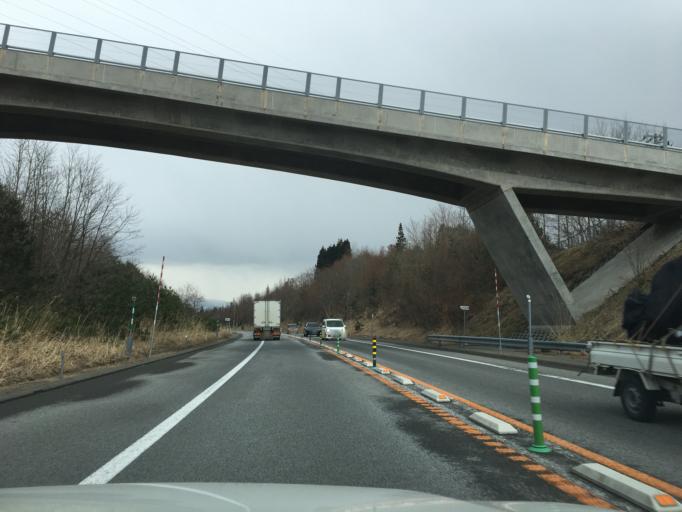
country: JP
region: Aomori
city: Aomori Shi
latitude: 40.7990
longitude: 140.7011
